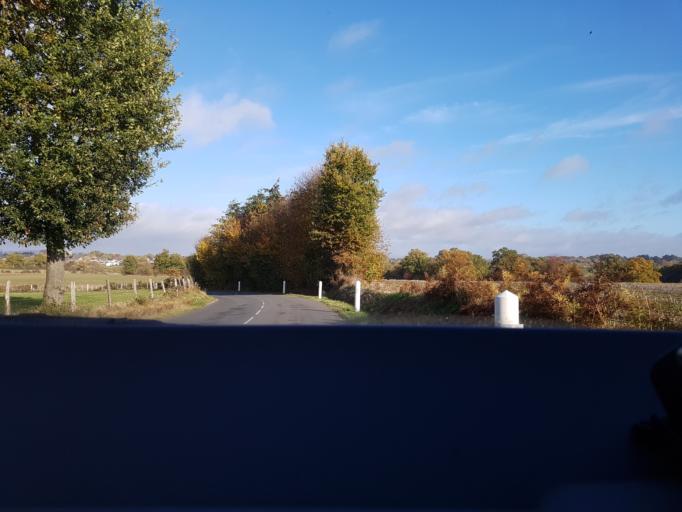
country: FR
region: Pays de la Loire
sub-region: Departement de la Mayenne
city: Ambrieres-les-Vallees
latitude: 48.4059
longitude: -0.5633
